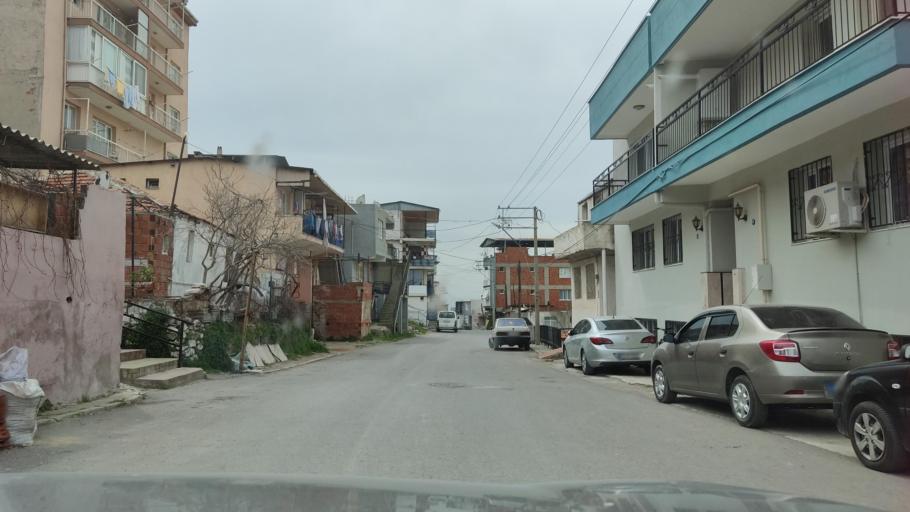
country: TR
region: Izmir
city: Karsiyaka
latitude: 38.5007
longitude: 27.0752
